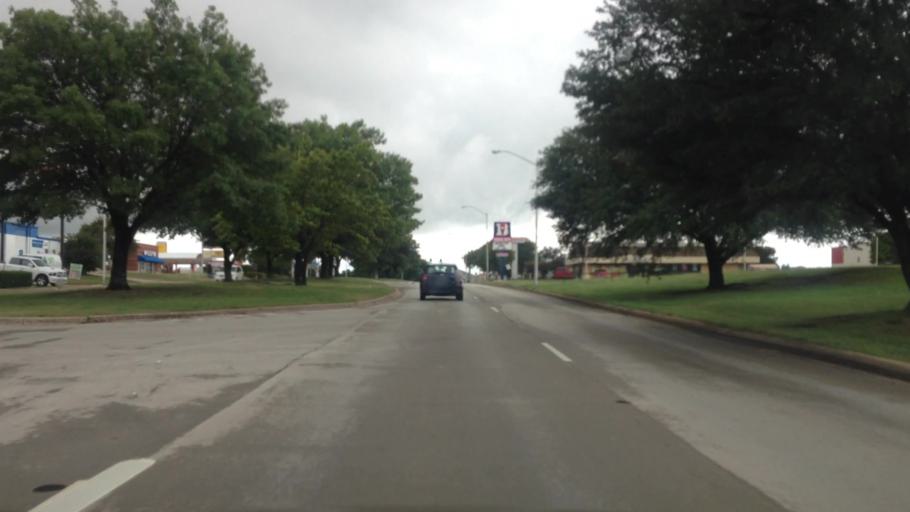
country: US
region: Texas
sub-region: Tarrant County
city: Edgecliff Village
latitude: 32.6430
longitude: -97.3960
